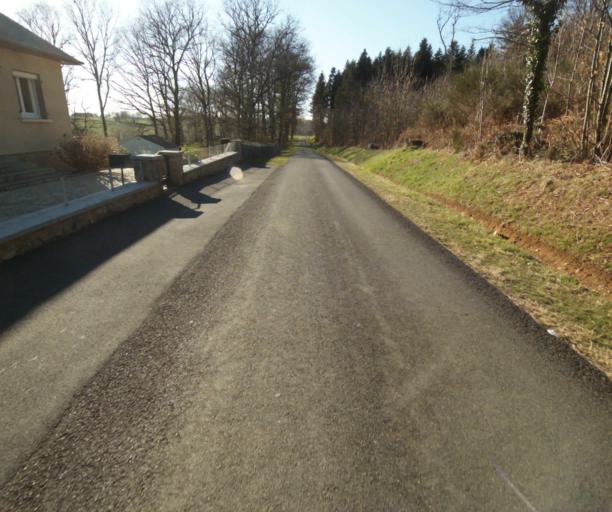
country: FR
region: Limousin
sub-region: Departement de la Correze
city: Seilhac
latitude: 45.3845
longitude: 1.6986
